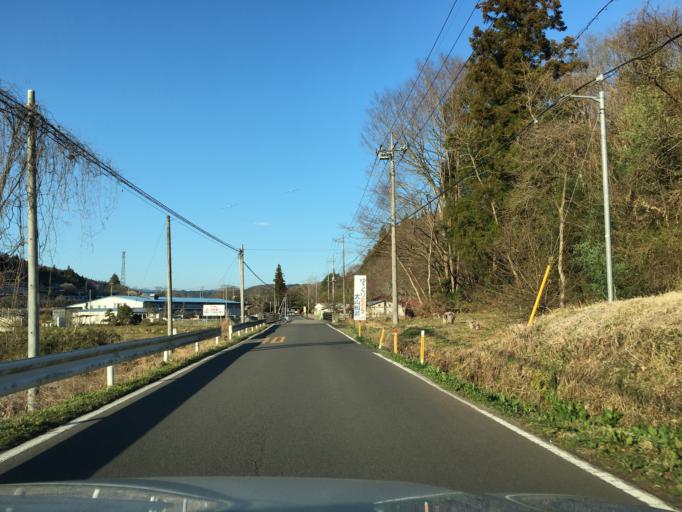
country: JP
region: Tochigi
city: Karasuyama
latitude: 36.7650
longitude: 140.2038
